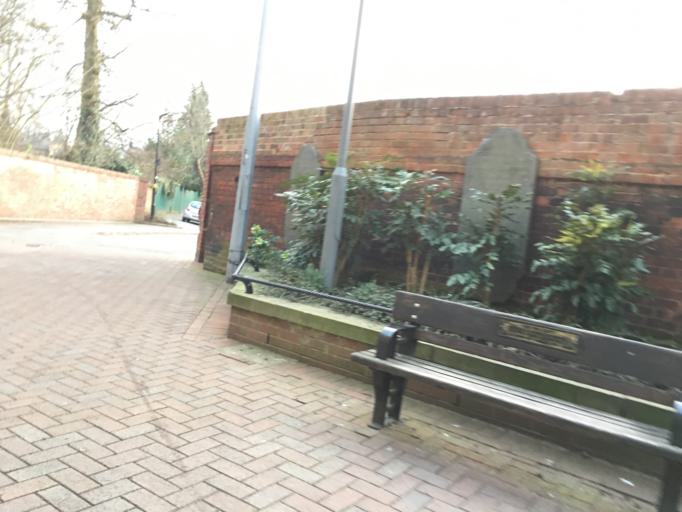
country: GB
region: England
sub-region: Warwickshire
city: Rugby
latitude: 52.3726
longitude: -1.2617
